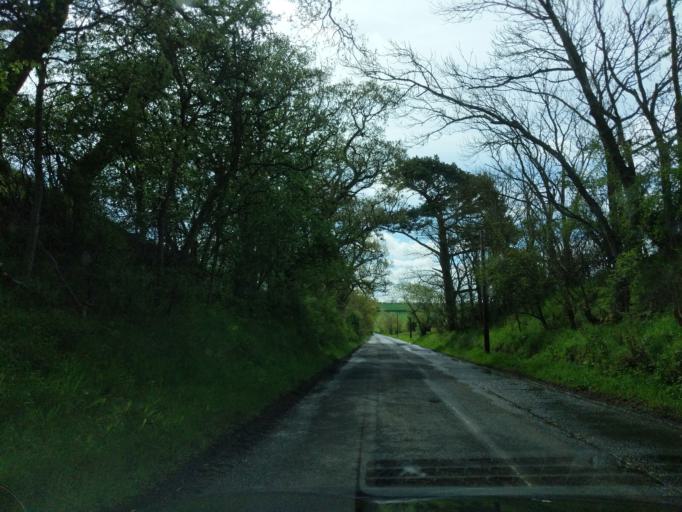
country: GB
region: Scotland
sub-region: The Scottish Borders
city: Saint Boswells
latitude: 55.6298
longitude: -2.5788
